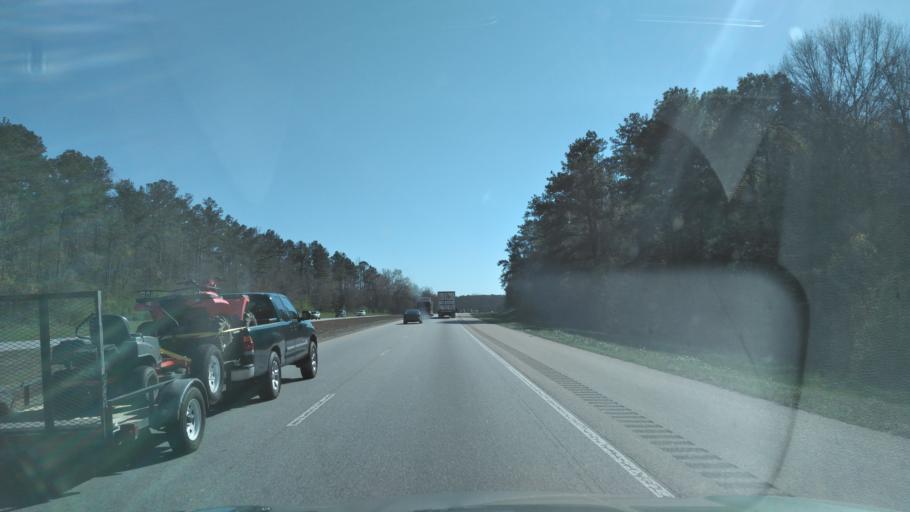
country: US
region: Alabama
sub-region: Lowndes County
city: Fort Deposit
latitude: 32.0363
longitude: -86.5078
